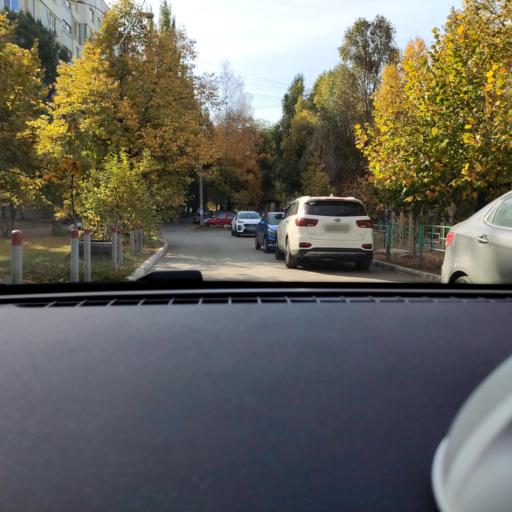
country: RU
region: Samara
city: Samara
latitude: 53.2657
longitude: 50.2232
